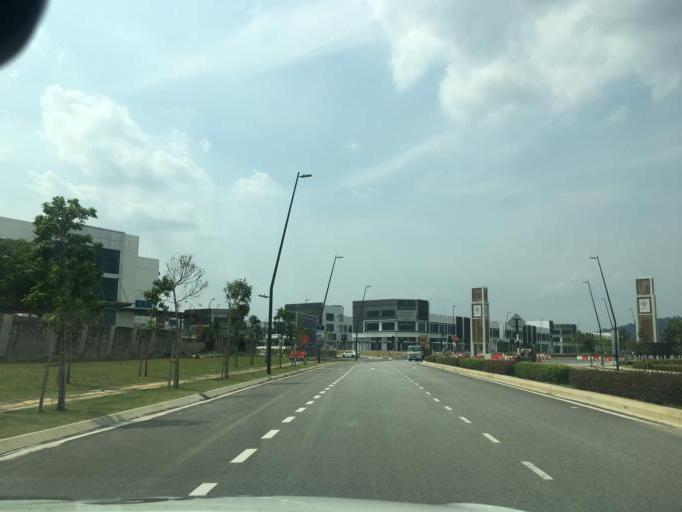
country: MY
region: Selangor
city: Shah Alam
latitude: 3.0845
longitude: 101.4764
